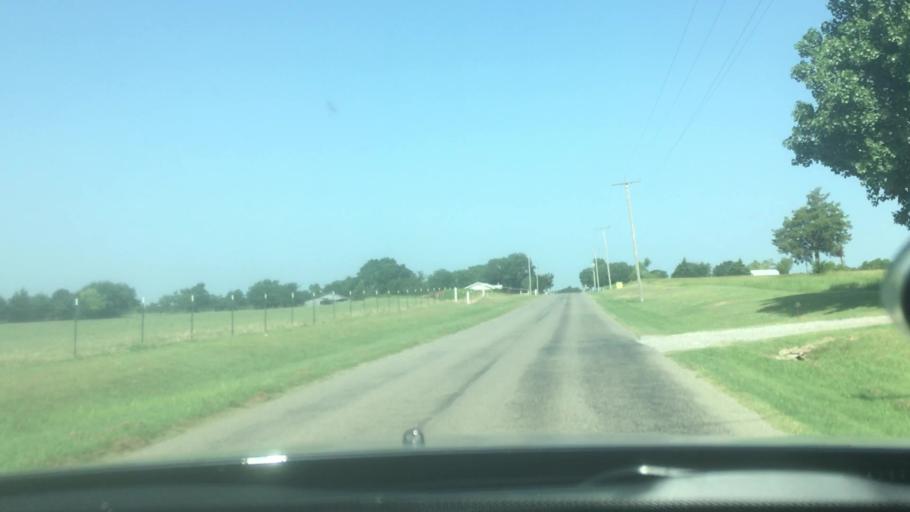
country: US
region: Oklahoma
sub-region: Bryan County
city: Calera
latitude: 33.9397
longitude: -96.4373
